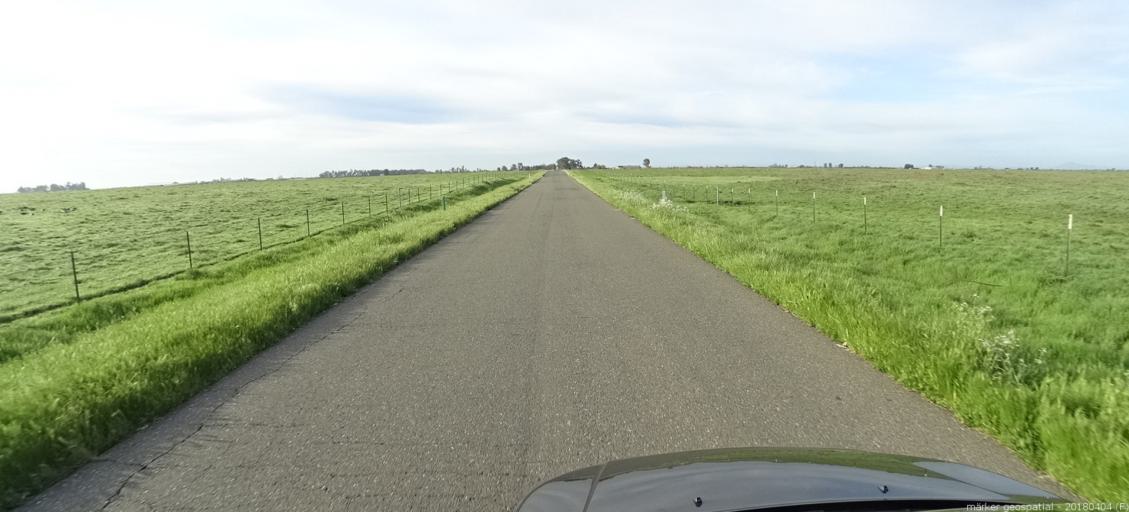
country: US
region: California
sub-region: Sacramento County
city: Wilton
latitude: 38.3495
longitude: -121.2976
